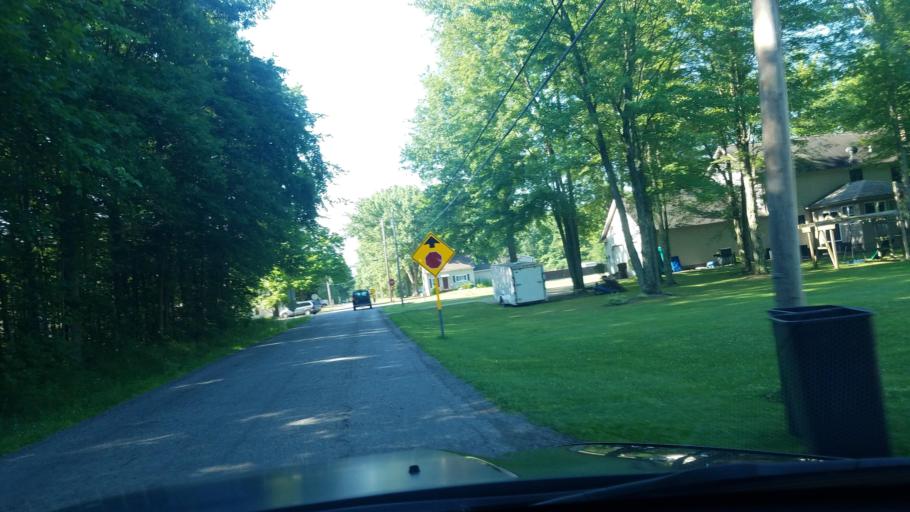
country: US
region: Ohio
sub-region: Trumbull County
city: Champion Heights
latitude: 41.3090
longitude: -80.8303
